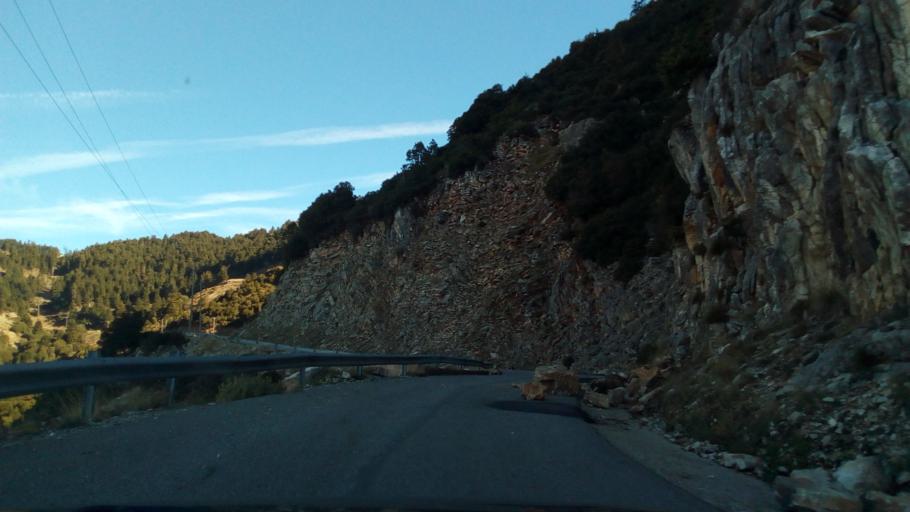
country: GR
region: West Greece
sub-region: Nomos Aitolias kai Akarnanias
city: Nafpaktos
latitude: 38.5220
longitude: 21.8484
